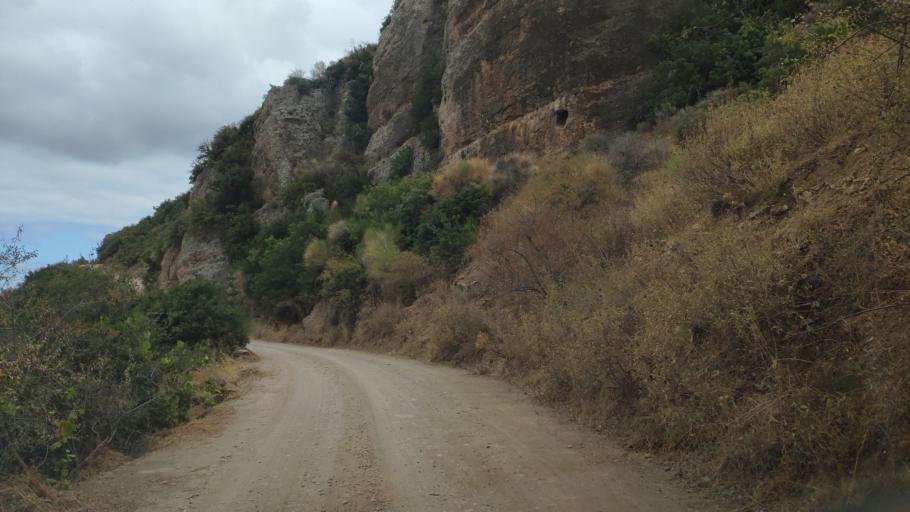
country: GR
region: West Greece
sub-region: Nomos Achaias
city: Temeni
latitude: 38.1593
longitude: 22.1421
